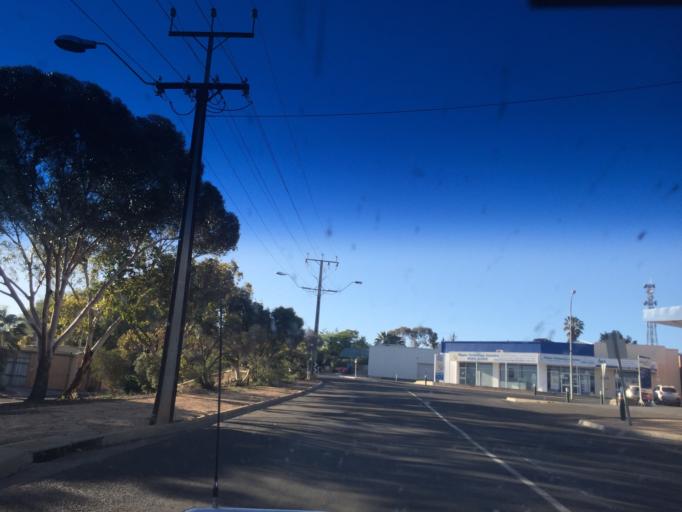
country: AU
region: South Australia
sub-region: Berri and Barmera
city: Berri
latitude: -34.2867
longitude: 140.5995
